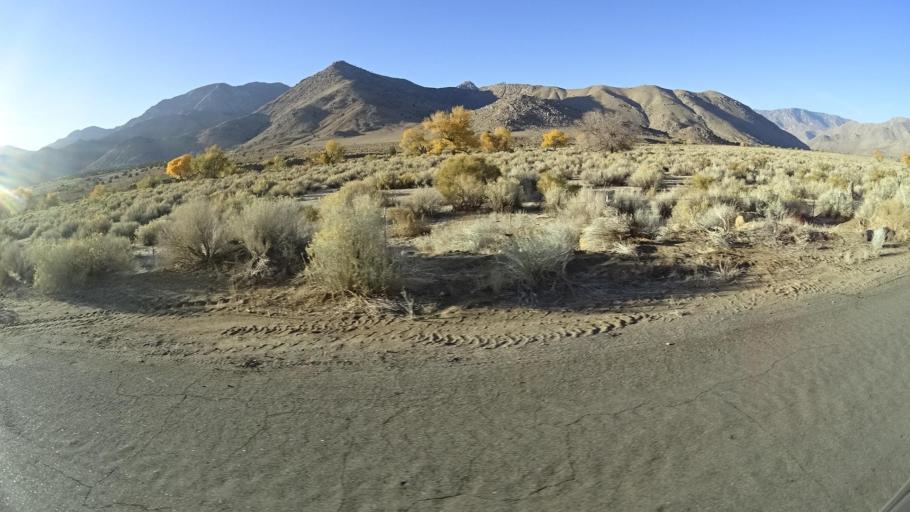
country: US
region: California
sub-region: Kern County
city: Weldon
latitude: 35.5816
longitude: -118.2470
